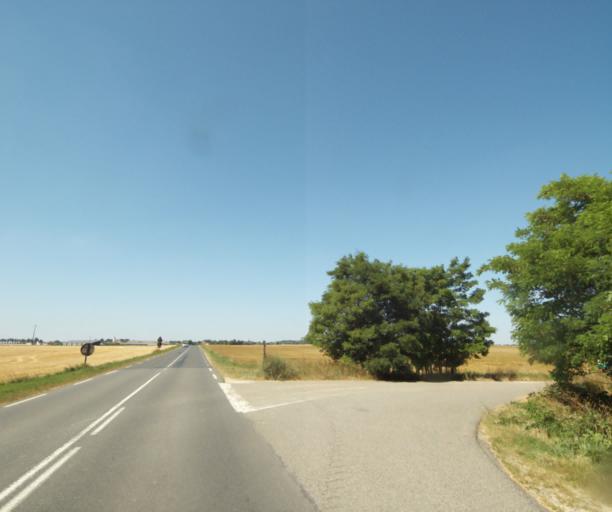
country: FR
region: Ile-de-France
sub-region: Departement de Seine-et-Marne
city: La Chapelle-la-Reine
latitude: 48.3021
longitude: 2.5736
